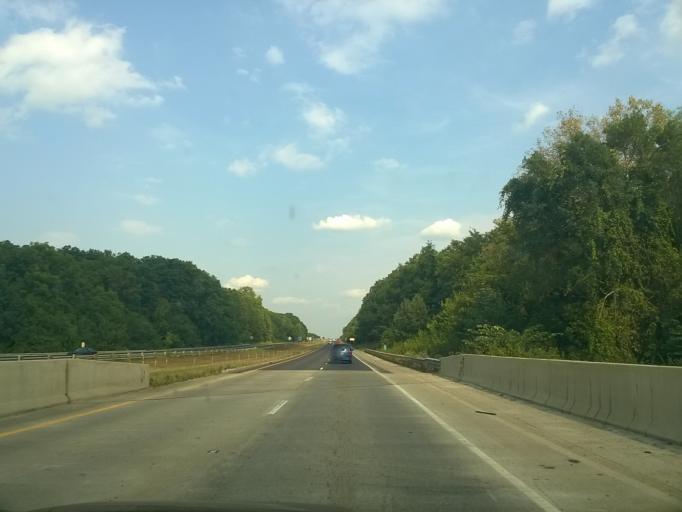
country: US
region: Indiana
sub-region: Vigo County
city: Terre Haute
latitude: 39.4306
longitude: -87.3729
